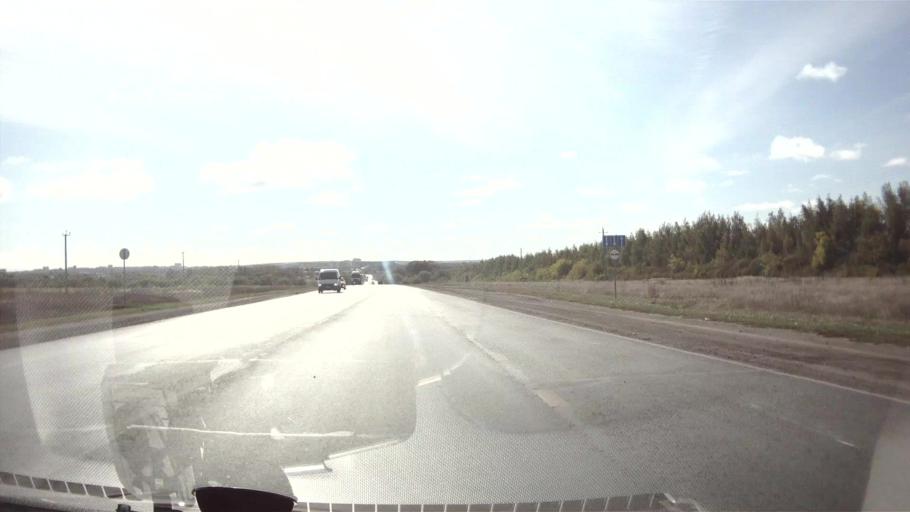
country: RU
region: Ulyanovsk
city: Isheyevka
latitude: 54.3109
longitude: 48.2364
